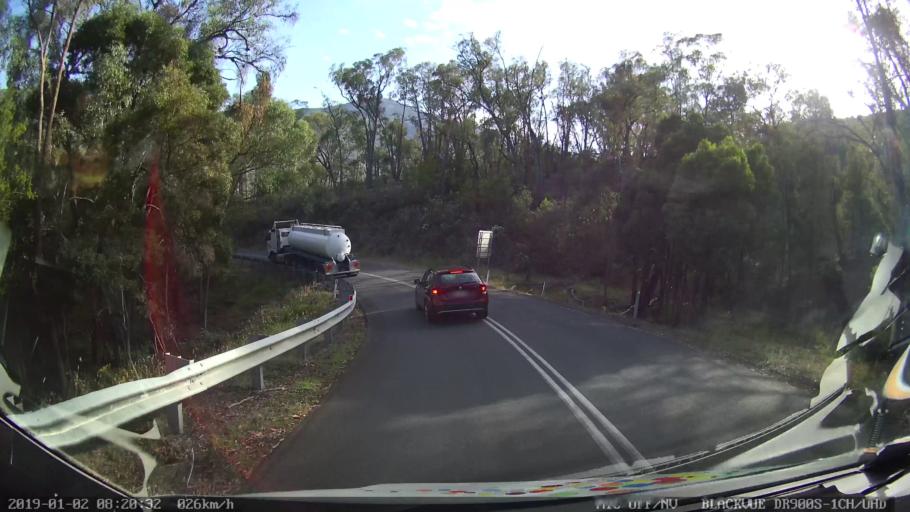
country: AU
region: New South Wales
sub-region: Tumut Shire
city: Tumut
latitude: -35.5720
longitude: 148.3241
